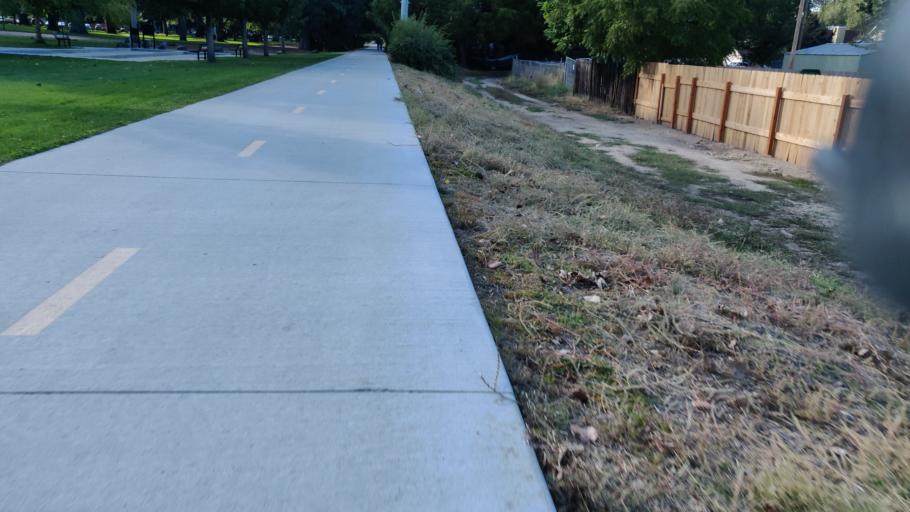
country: US
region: Idaho
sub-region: Ada County
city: Boise
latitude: 43.6024
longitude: -116.1806
